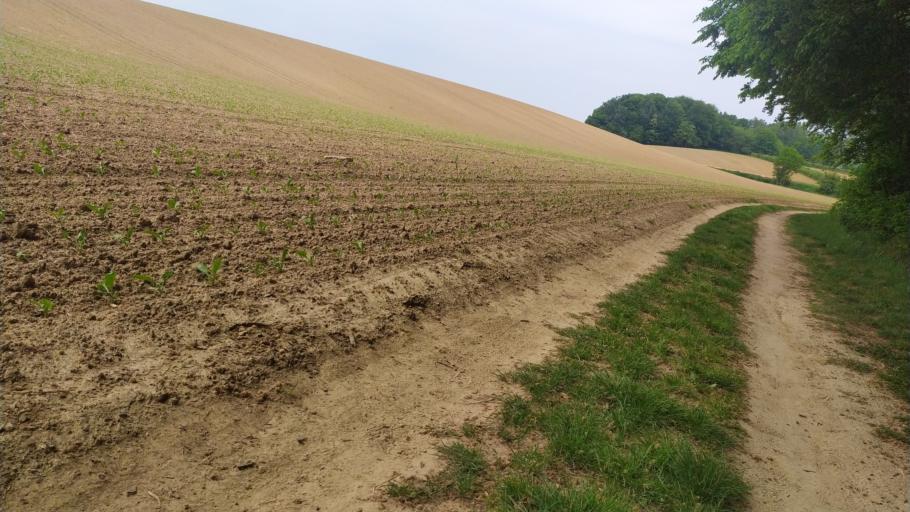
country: BE
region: Flanders
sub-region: Provincie Vlaams-Brabant
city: Huldenberg
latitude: 50.8268
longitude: 4.5921
